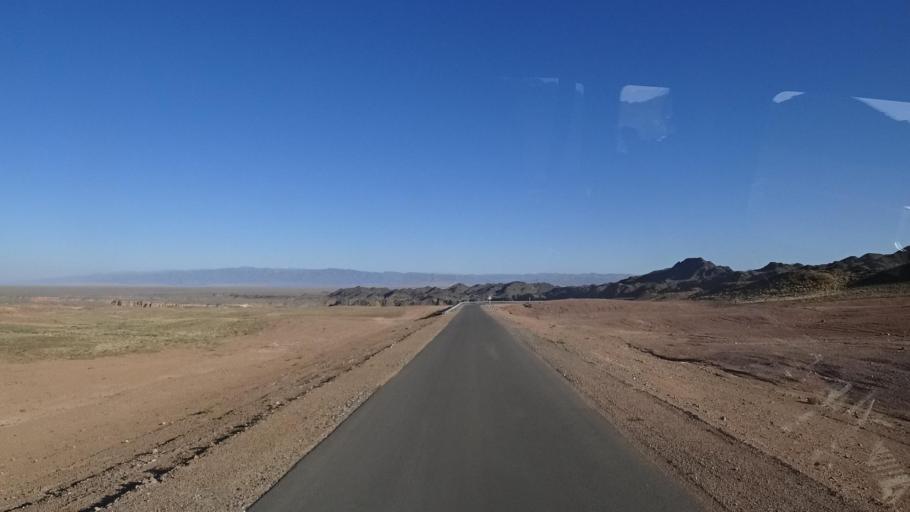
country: KZ
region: Almaty Oblysy
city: Kegen
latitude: 43.3595
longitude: 79.0512
